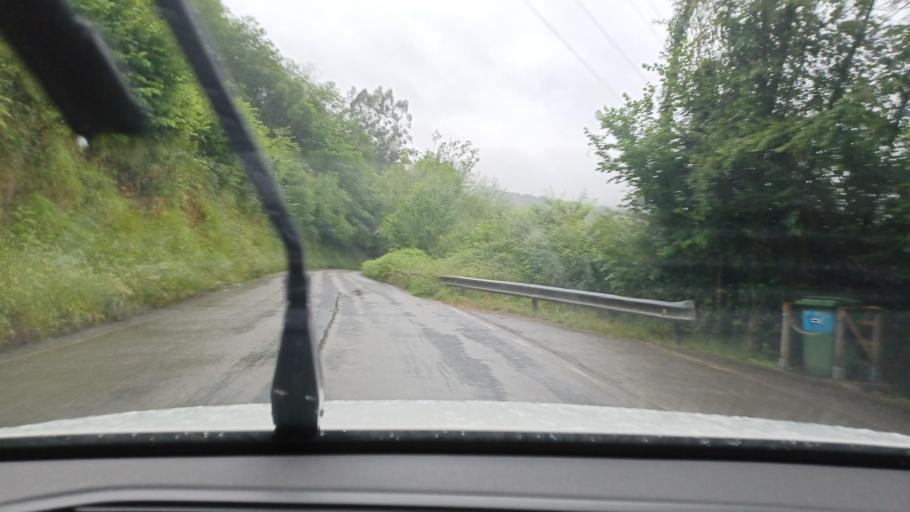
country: ES
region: Asturias
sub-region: Province of Asturias
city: Castandiello
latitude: 43.3084
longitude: -5.9038
